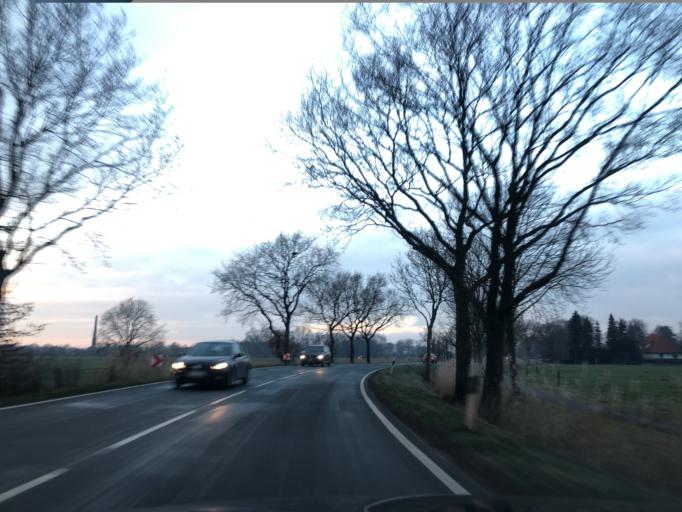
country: DE
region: Lower Saxony
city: Lemwerder
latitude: 53.1375
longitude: 8.5970
